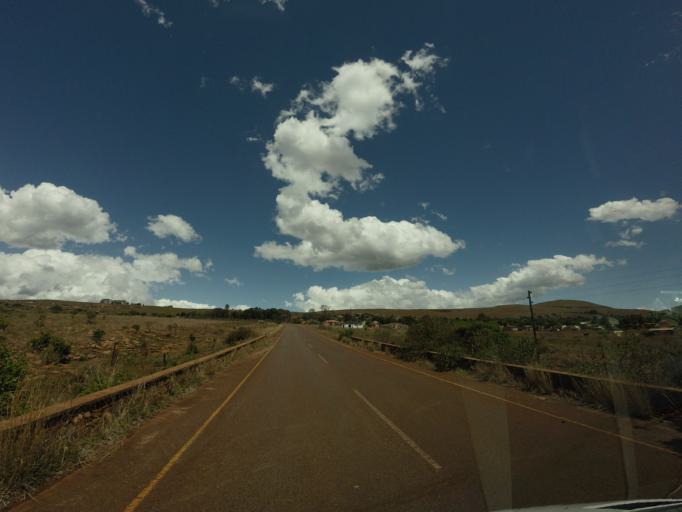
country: ZA
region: Limpopo
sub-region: Mopani District Municipality
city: Hoedspruit
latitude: -24.6106
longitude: 30.7976
